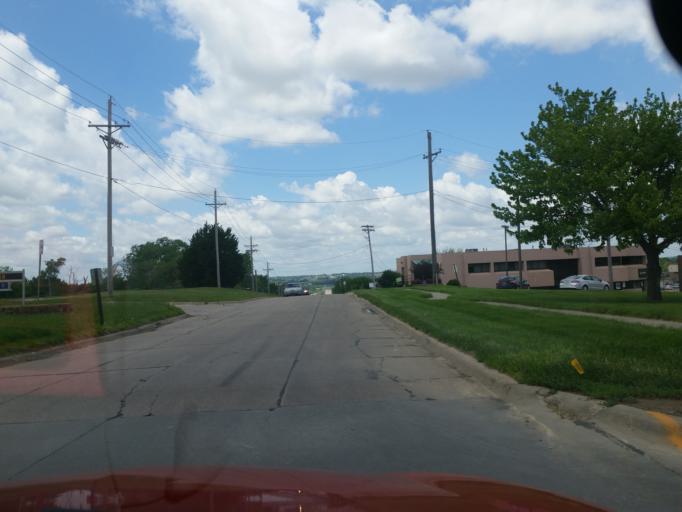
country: US
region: Nebraska
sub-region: Sarpy County
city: Bellevue
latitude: 41.1403
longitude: -95.9099
